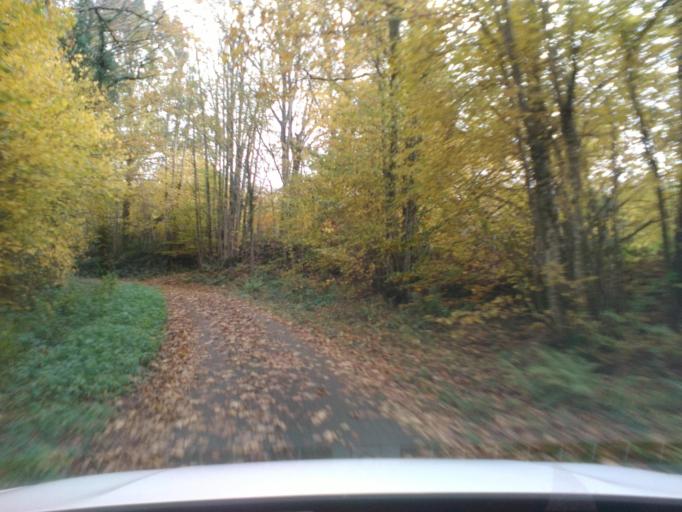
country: FR
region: Lorraine
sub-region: Departement des Vosges
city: Senones
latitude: 48.3349
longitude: 7.0264
